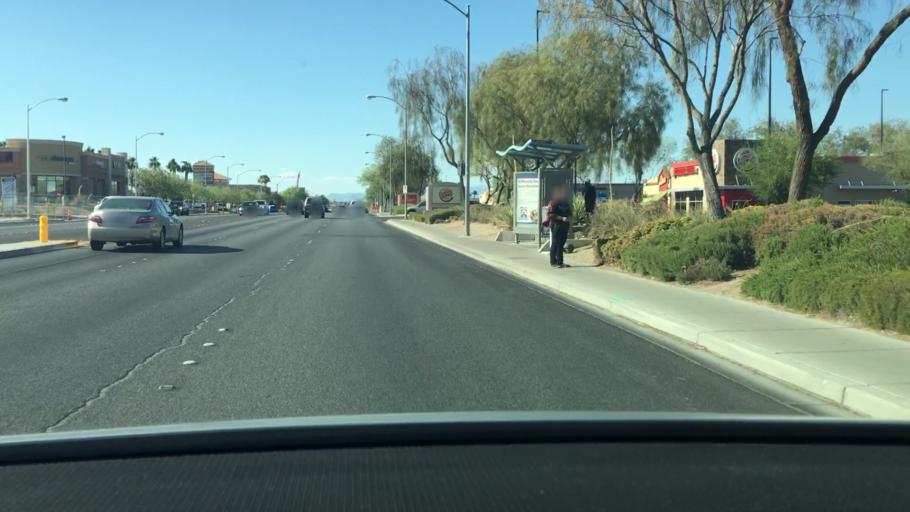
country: US
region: Nevada
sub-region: Clark County
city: Summerlin South
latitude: 36.0935
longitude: -115.2972
